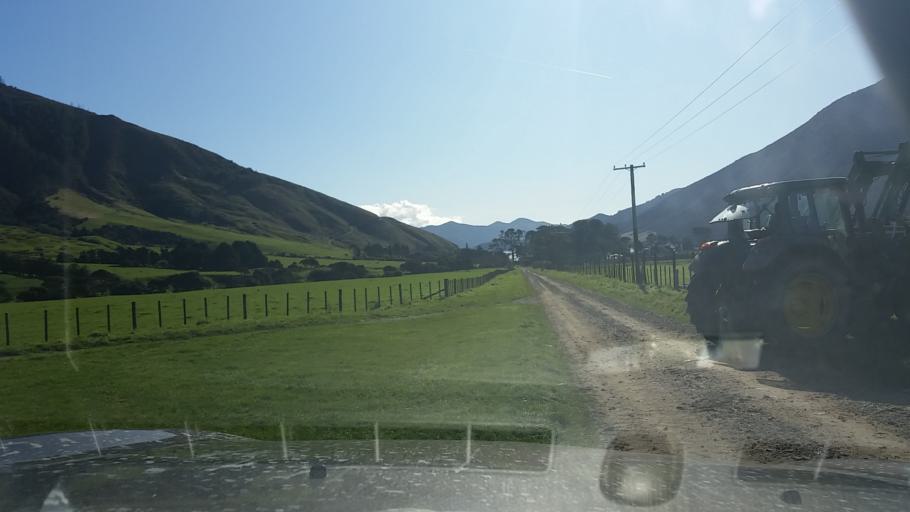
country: NZ
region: Marlborough
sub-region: Marlborough District
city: Picton
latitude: -41.1206
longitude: 174.0378
